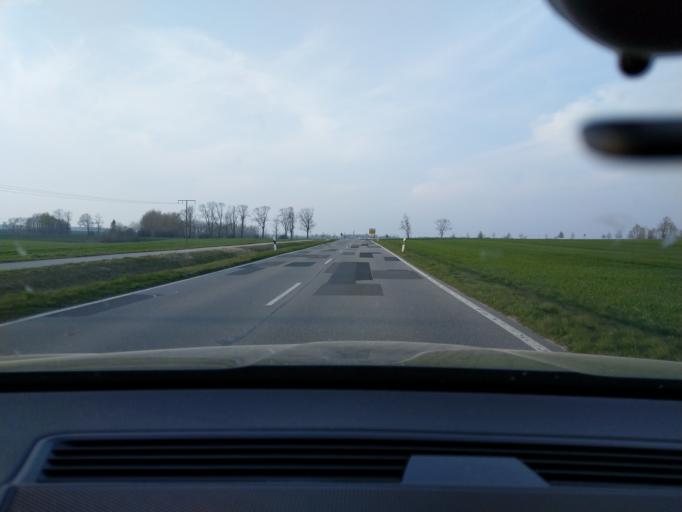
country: DE
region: Mecklenburg-Vorpommern
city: Prohn
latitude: 54.3463
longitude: 13.0296
